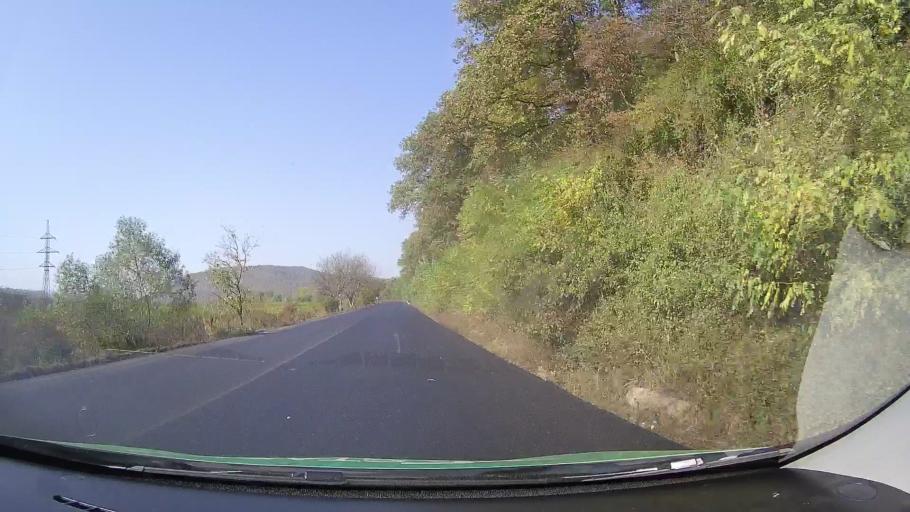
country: RO
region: Hunedoara
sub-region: Comuna Zam
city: Zam
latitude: 46.0179
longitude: 22.4136
